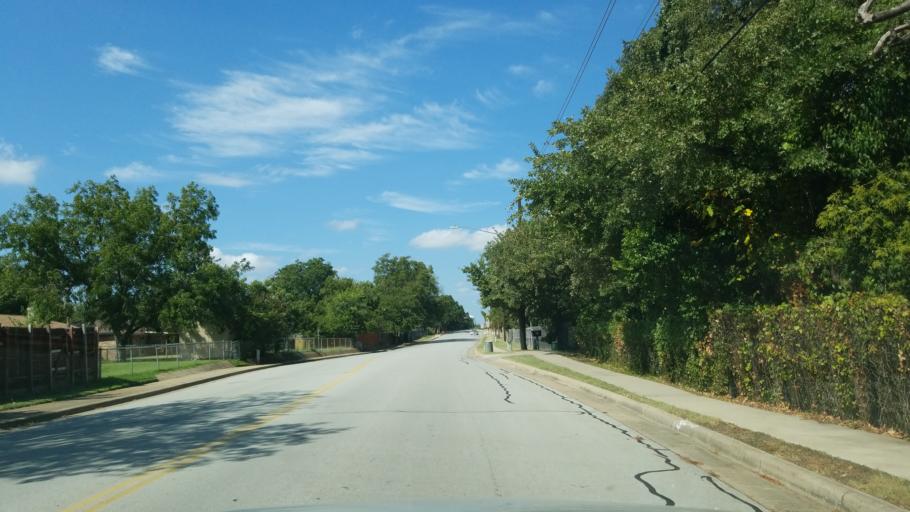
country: US
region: Texas
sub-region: Tarrant County
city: Euless
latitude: 32.8591
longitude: -97.0906
